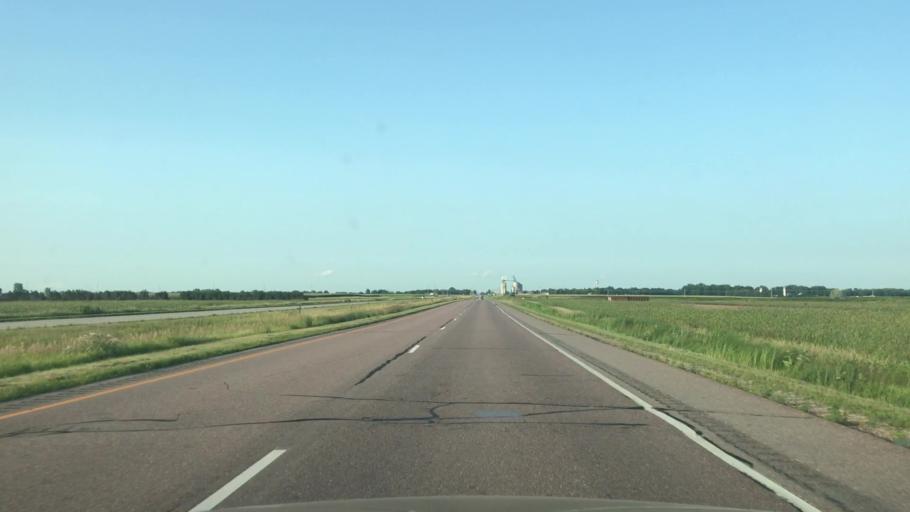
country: US
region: Minnesota
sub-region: Jackson County
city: Lakefield
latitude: 43.7810
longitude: -95.3445
